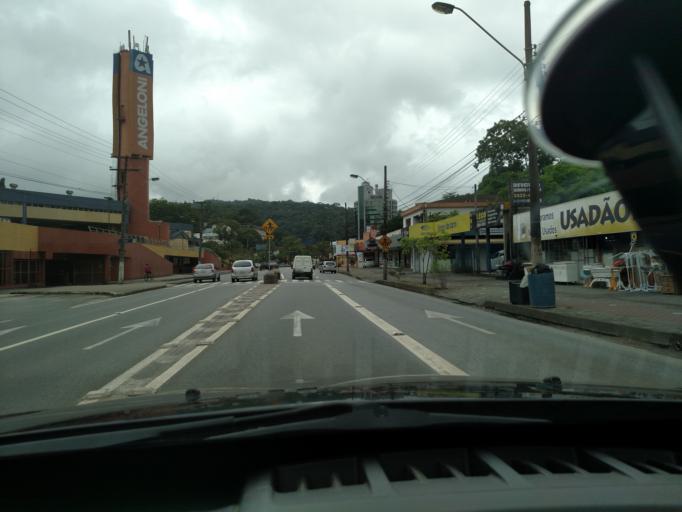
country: BR
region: Santa Catarina
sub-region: Blumenau
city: Blumenau
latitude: -26.9251
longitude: -49.0584
